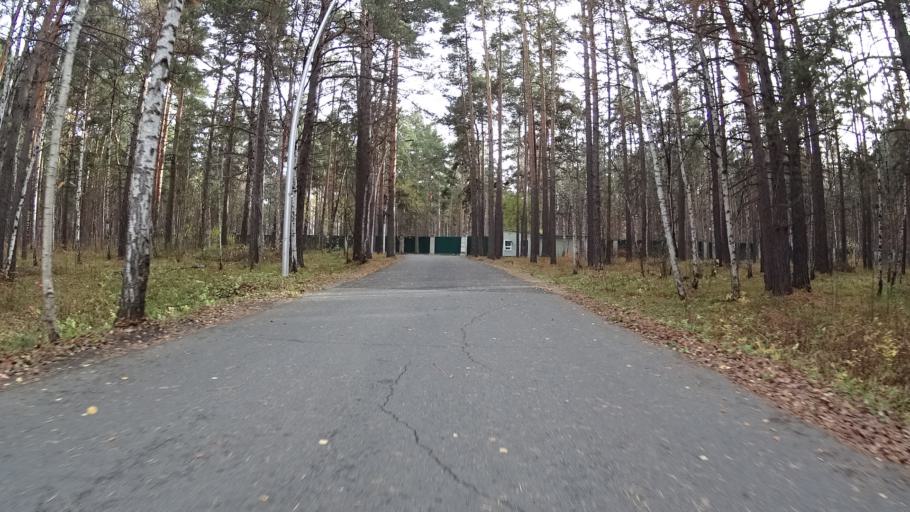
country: RU
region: Chelyabinsk
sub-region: Gorod Chelyabinsk
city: Chelyabinsk
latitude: 55.1381
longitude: 61.3512
